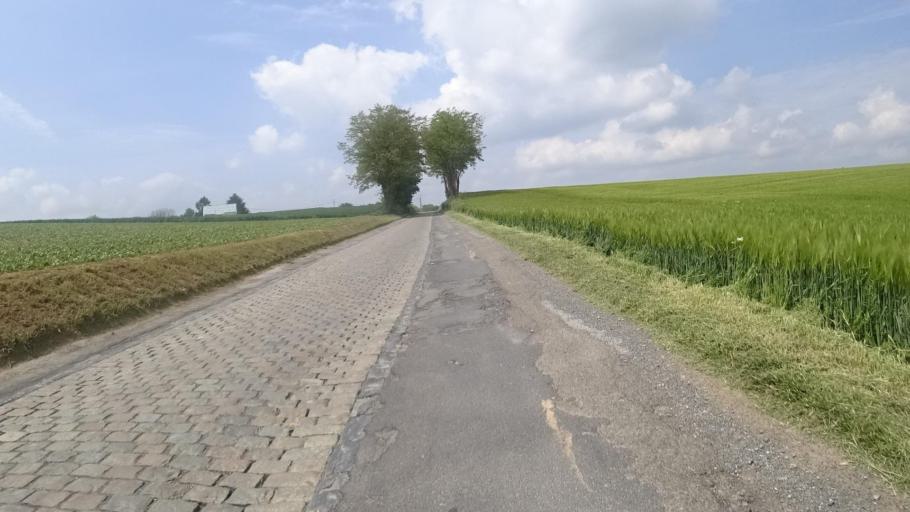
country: BE
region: Wallonia
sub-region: Province du Brabant Wallon
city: Louvain-la-Neuve
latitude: 50.6828
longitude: 4.6425
